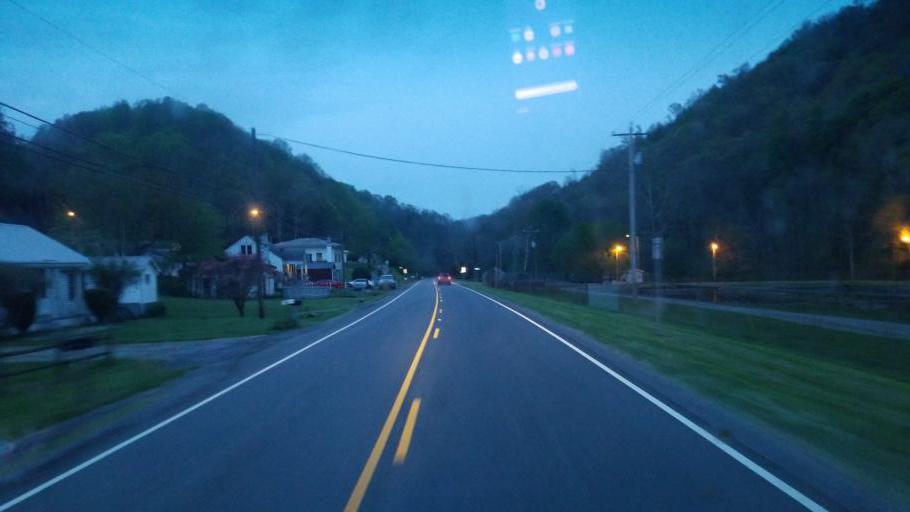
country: US
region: Virginia
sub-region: Smyth County
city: Marion
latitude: 36.8235
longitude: -81.4793
